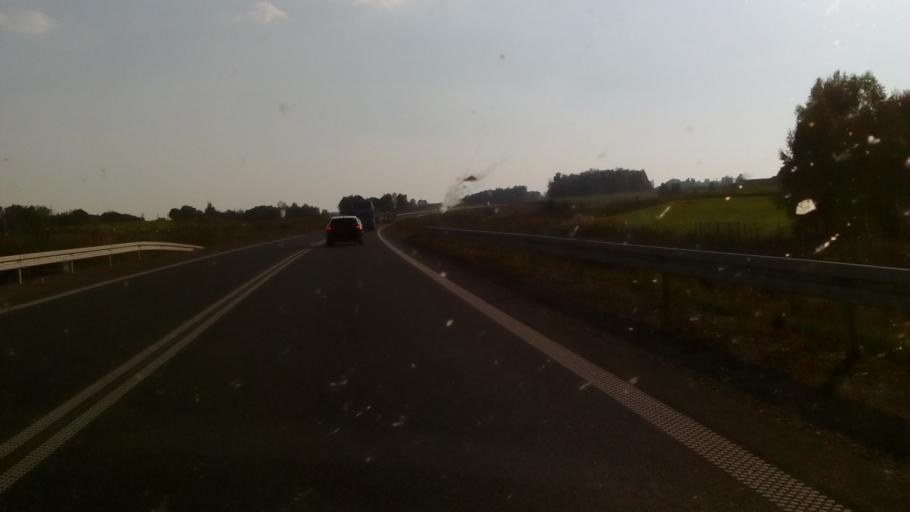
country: PL
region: Podlasie
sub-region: Powiat grajewski
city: Rajgrod
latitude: 53.7645
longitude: 22.8295
